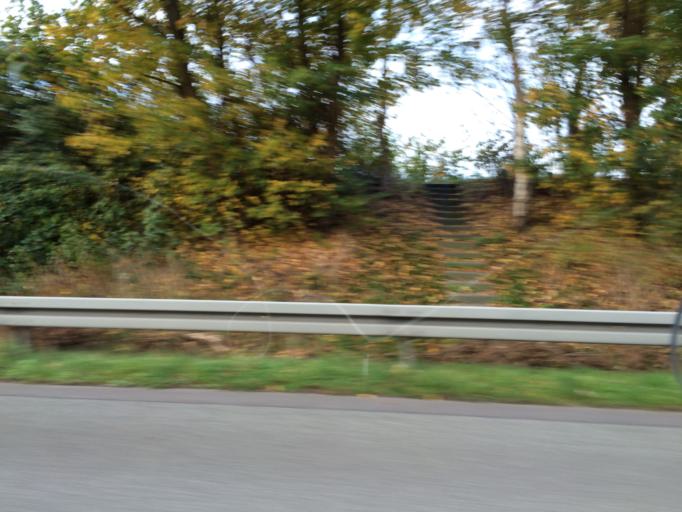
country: DE
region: North Rhine-Westphalia
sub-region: Regierungsbezirk Munster
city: Dulmen
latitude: 51.8394
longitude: 7.2478
